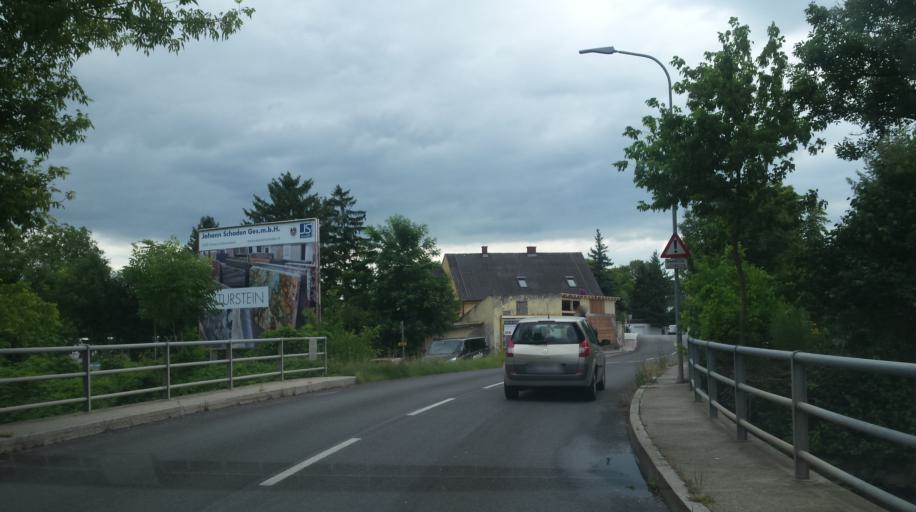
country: AT
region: Lower Austria
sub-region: Politischer Bezirk Wien-Umgebung
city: Zwolfaxing
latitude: 48.1143
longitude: 16.4599
